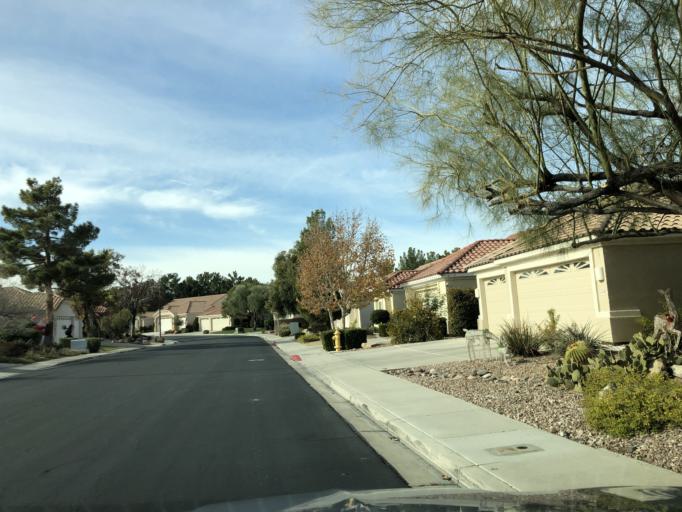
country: US
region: Nevada
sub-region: Clark County
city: Whitney
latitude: 36.0143
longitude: -115.0848
